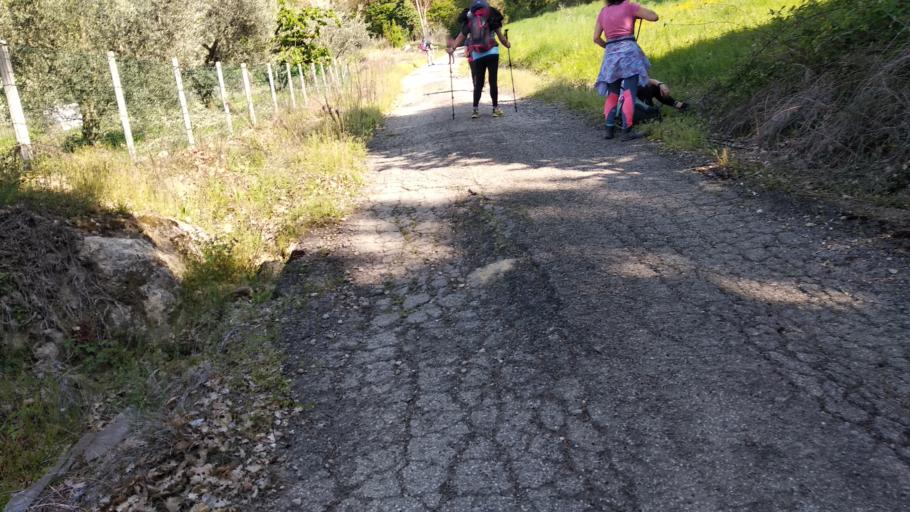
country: IT
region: Emilia-Romagna
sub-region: Provincia di Ravenna
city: Fognano
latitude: 44.2304
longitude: 11.7203
